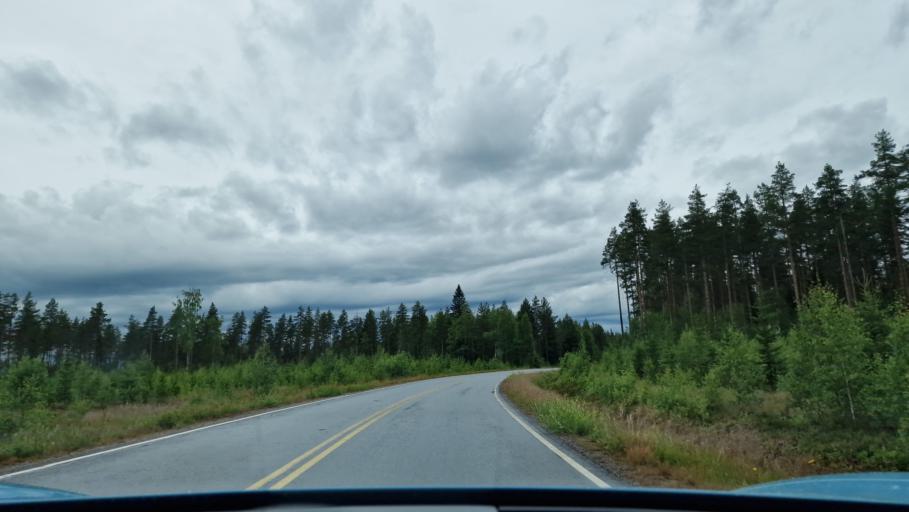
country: FI
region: Central Finland
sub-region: Saarijaervi-Viitasaari
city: Pylkoenmaeki
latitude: 62.6712
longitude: 24.5132
